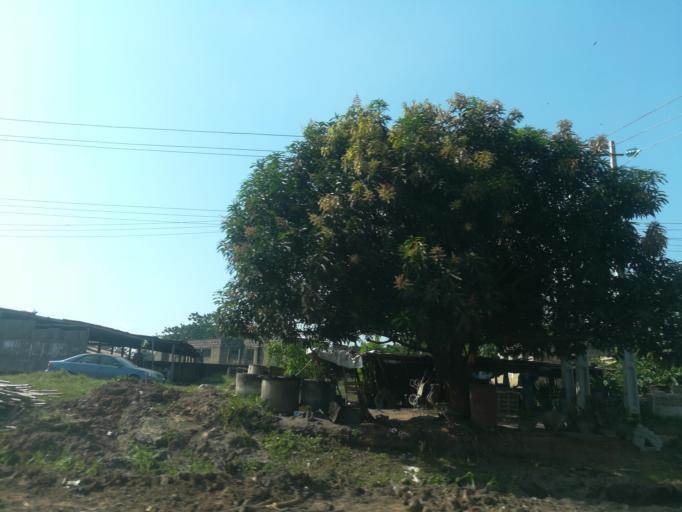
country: NG
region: Ogun
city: Abeokuta
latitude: 7.1432
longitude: 3.3153
